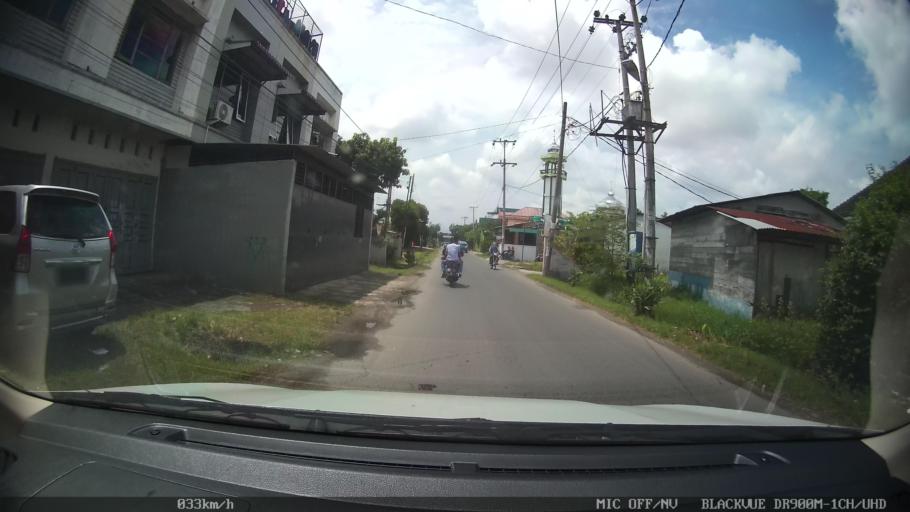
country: ID
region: North Sumatra
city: Medan
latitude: 3.6036
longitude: 98.7470
